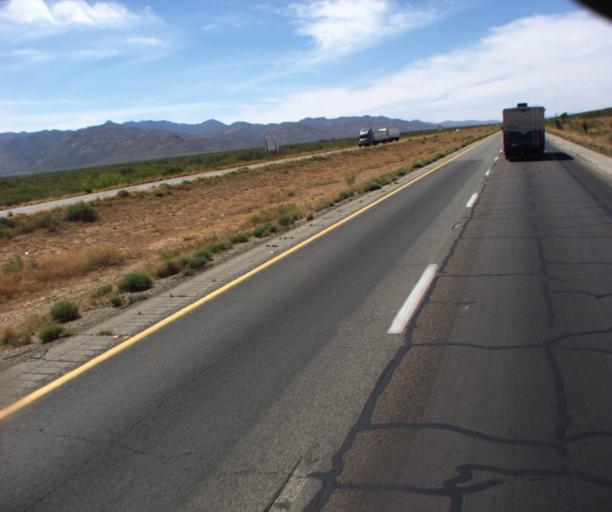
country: US
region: Arizona
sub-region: Cochise County
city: Willcox
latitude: 32.3176
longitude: -109.4623
